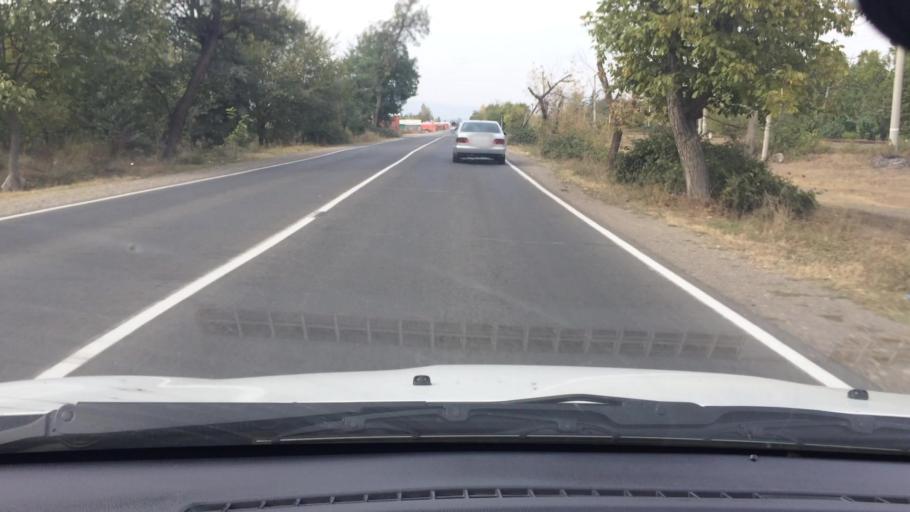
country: GE
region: Kvemo Kartli
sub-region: Marneuli
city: Marneuli
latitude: 41.4165
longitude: 44.8266
